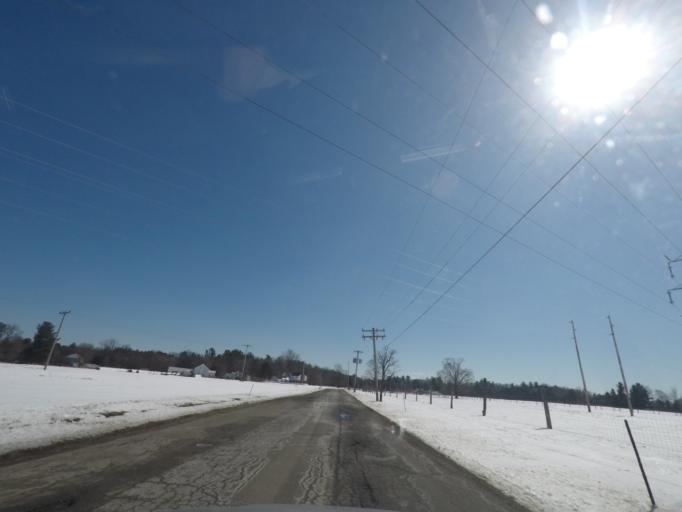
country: US
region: New York
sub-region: Saratoga County
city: Stillwater
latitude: 42.9115
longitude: -73.6089
